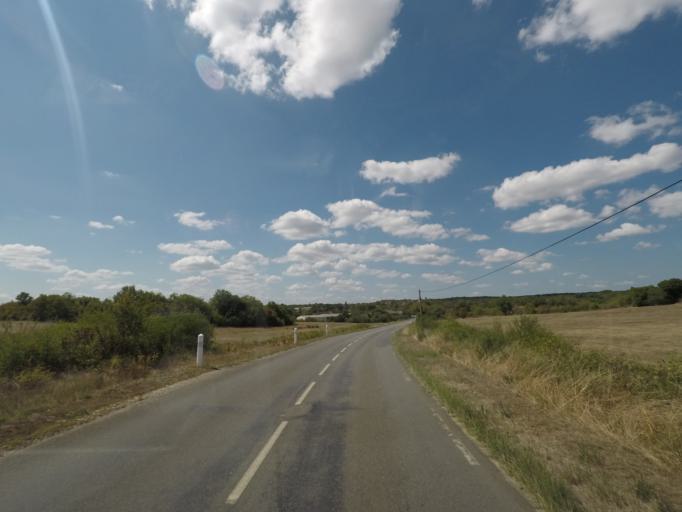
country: FR
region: Midi-Pyrenees
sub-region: Departement du Lot
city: Lacapelle-Marival
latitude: 44.6265
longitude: 1.8297
